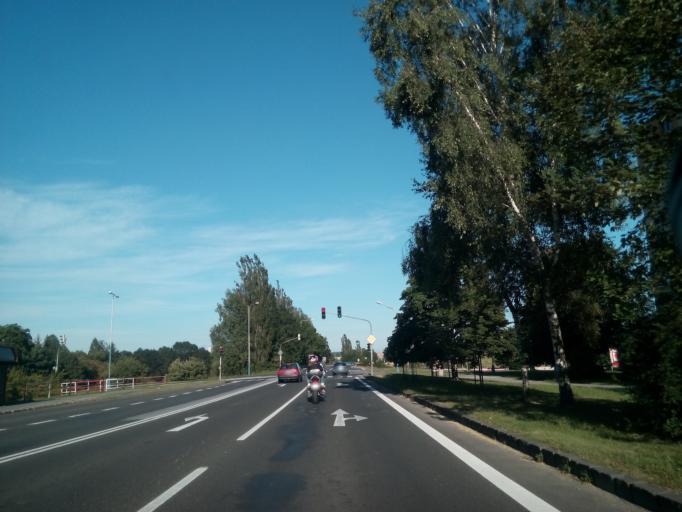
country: SK
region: Presovsky
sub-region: Okres Poprad
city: Poprad
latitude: 49.0500
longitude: 20.3043
